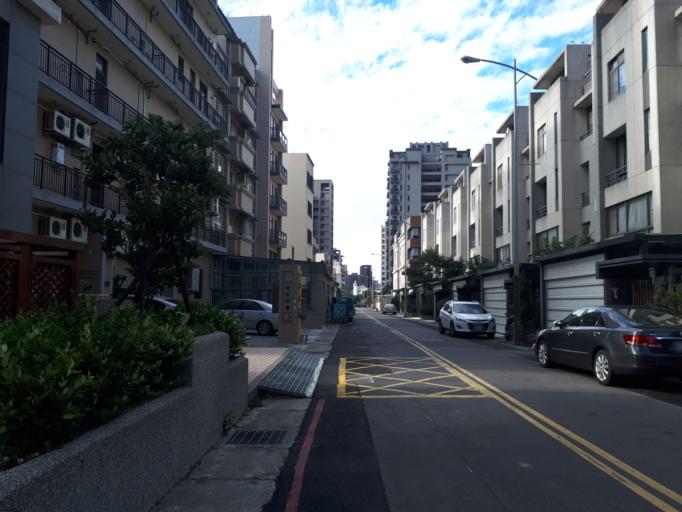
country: TW
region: Taiwan
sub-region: Hsinchu
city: Zhubei
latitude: 24.8017
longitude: 121.0350
